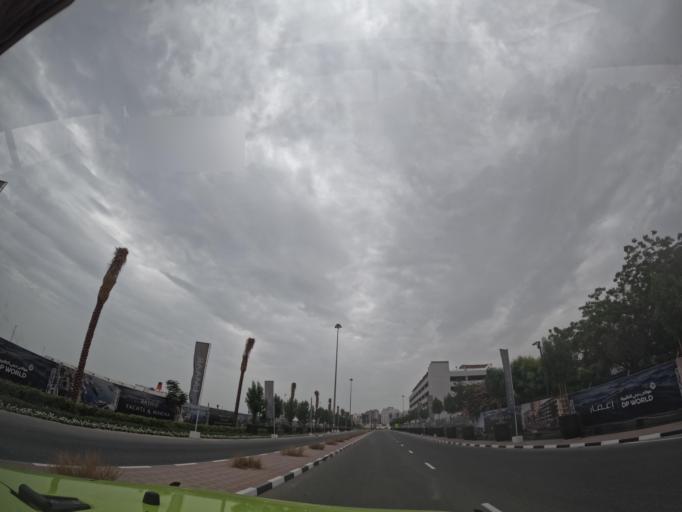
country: AE
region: Ash Shariqah
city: Sharjah
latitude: 25.2553
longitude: 55.2817
